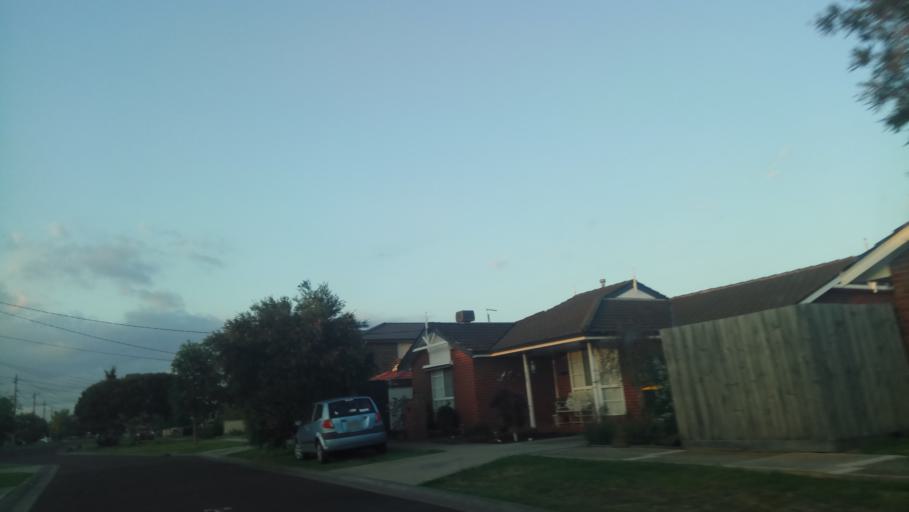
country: AU
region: Victoria
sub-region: Hobsons Bay
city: Altona Meadows
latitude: -37.8772
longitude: 144.7814
